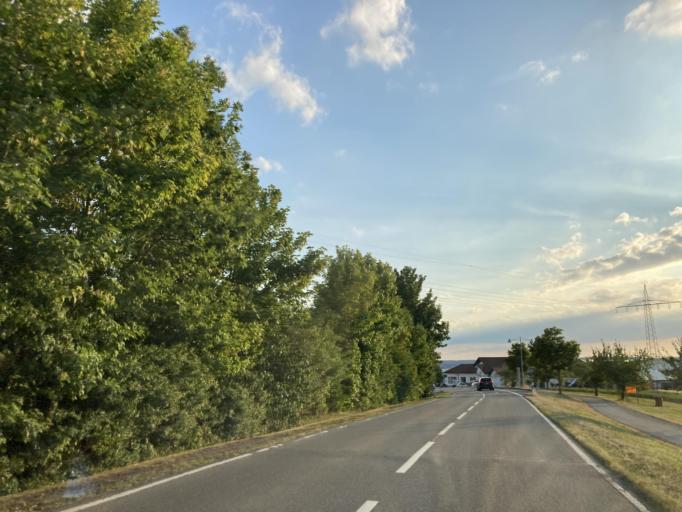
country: DE
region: Baden-Wuerttemberg
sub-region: Karlsruhe Region
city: Dornstetten
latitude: 48.4812
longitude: 8.4958
